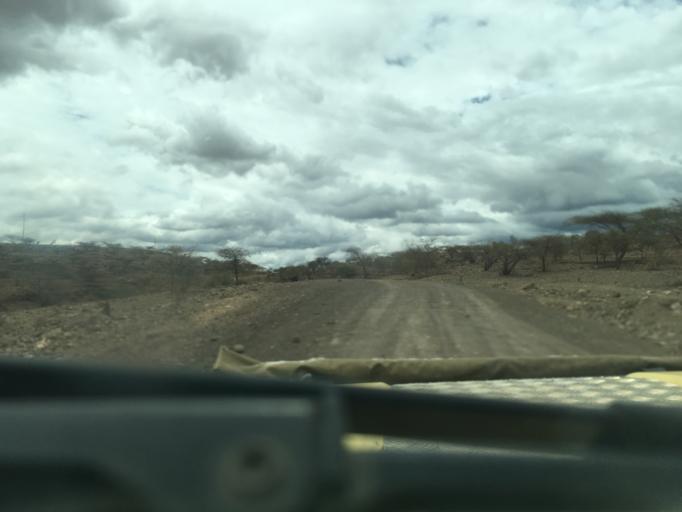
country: TZ
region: Arusha
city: Mto wa Mbu
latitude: -3.0958
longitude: 36.0185
